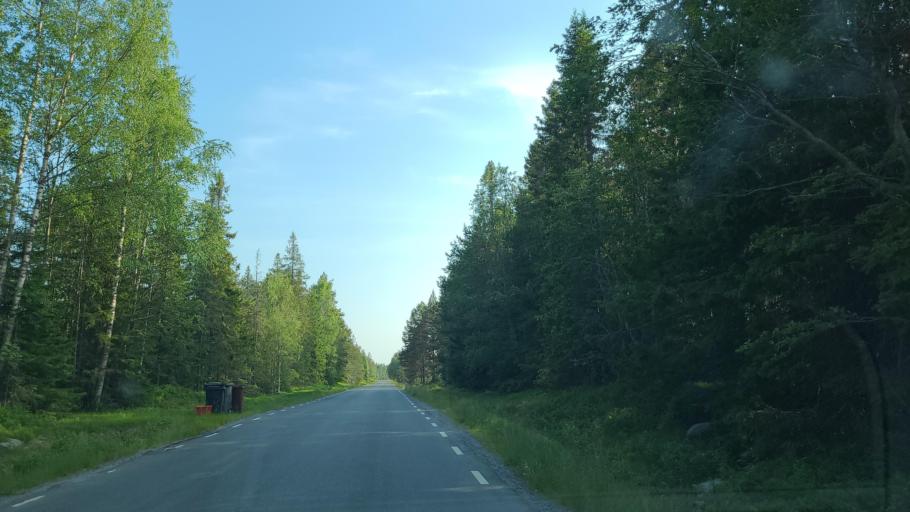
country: SE
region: Vaesterbotten
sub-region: Skelleftea Kommun
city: Burea
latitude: 64.4618
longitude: 21.5856
